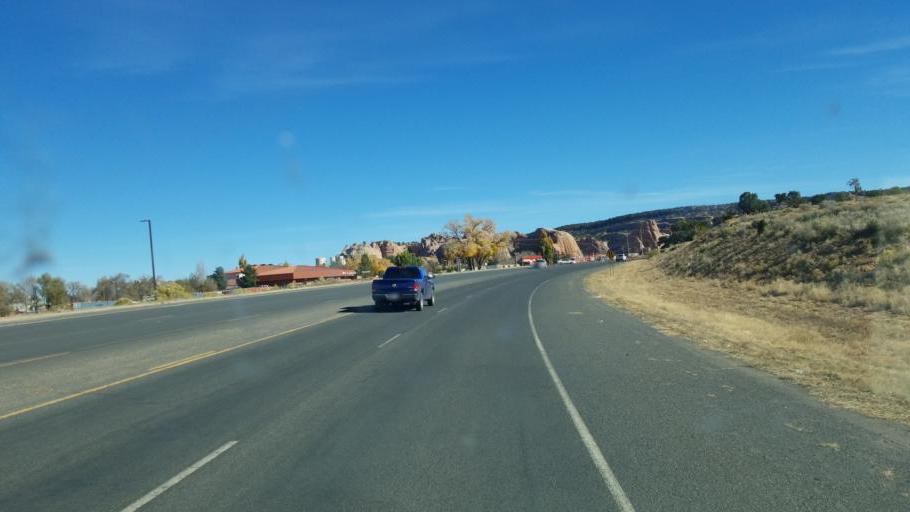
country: US
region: Arizona
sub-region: Apache County
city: Window Rock
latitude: 35.6749
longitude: -109.0556
